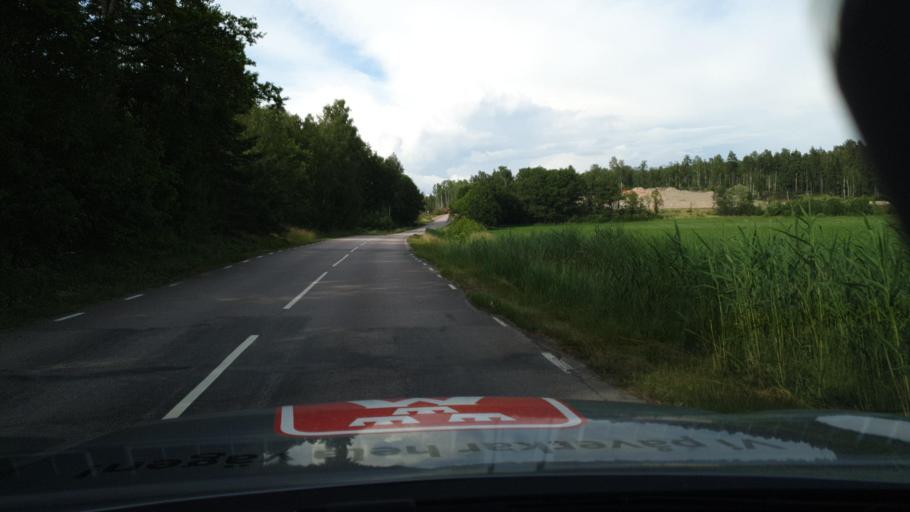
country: SE
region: Vaestmanland
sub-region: Hallstahammars Kommun
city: Kolback
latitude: 59.5282
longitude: 16.3163
